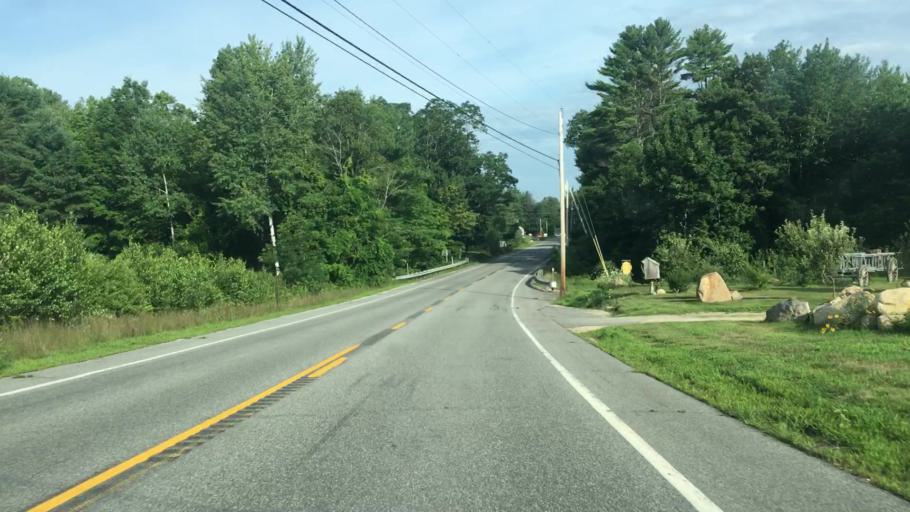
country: US
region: Maine
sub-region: York County
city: Cornish
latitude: 43.7871
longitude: -70.7646
